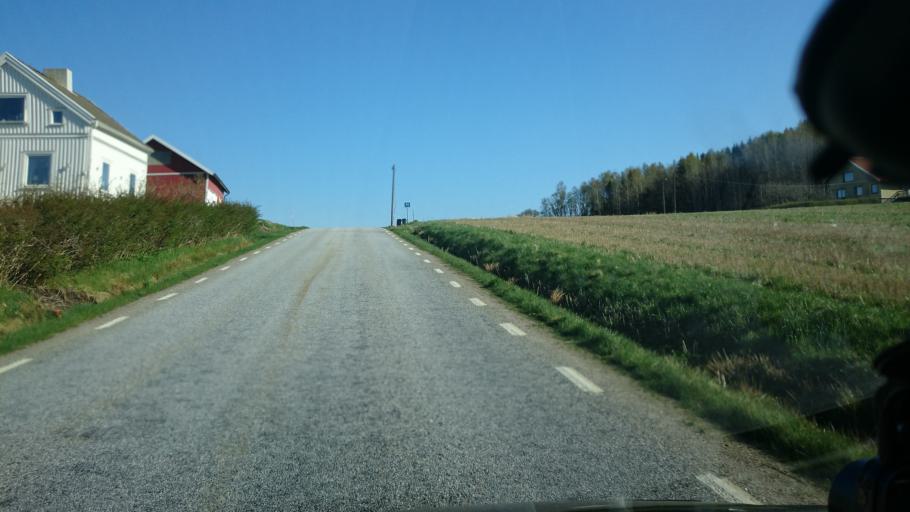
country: SE
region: Vaestra Goetaland
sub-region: Munkedals Kommun
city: Munkedal
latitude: 58.3852
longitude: 11.6625
